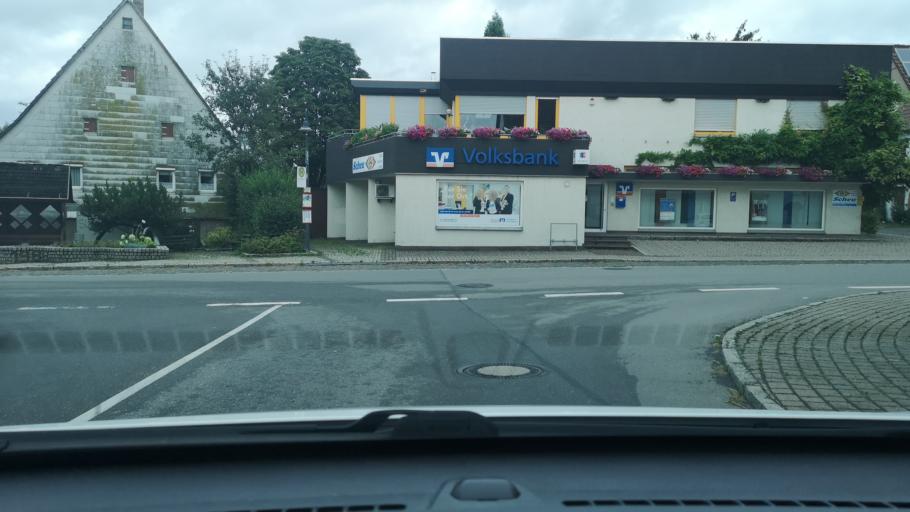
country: DE
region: Baden-Wuerttemberg
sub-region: Freiburg Region
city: Vohringen
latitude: 48.3366
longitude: 8.6611
